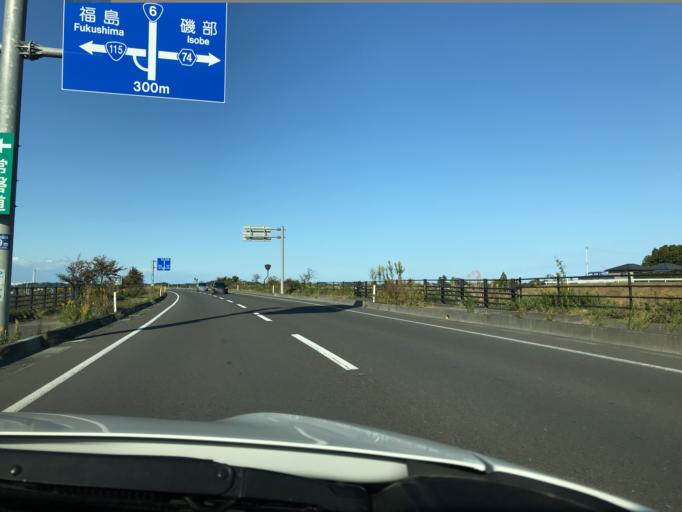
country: JP
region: Miyagi
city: Marumori
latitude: 37.7860
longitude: 140.9434
